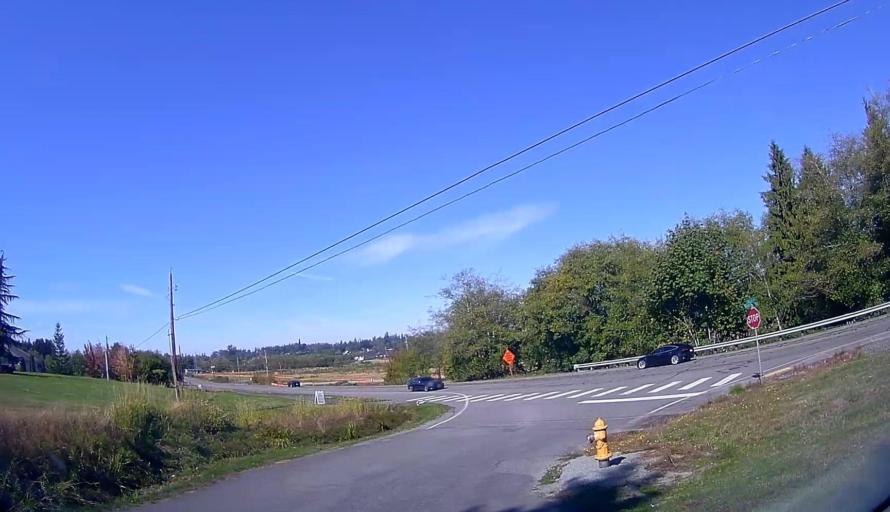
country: US
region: Washington
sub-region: Skagit County
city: Big Lake
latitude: 48.4344
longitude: -122.2787
